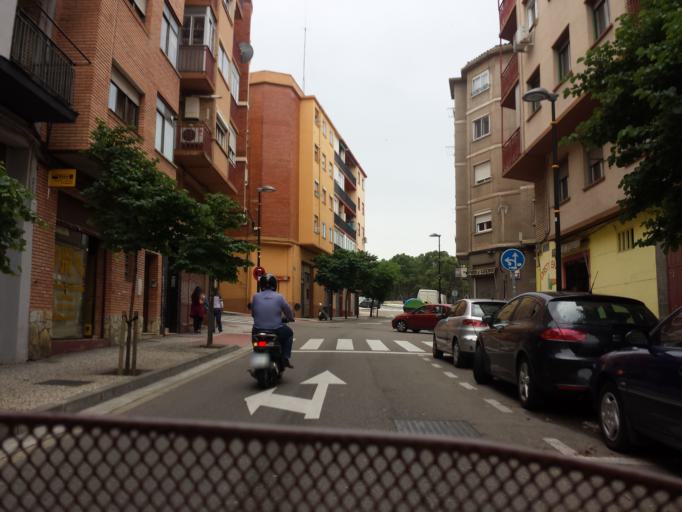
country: ES
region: Aragon
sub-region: Provincia de Zaragoza
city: Zaragoza
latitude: 41.6269
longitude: -0.8833
